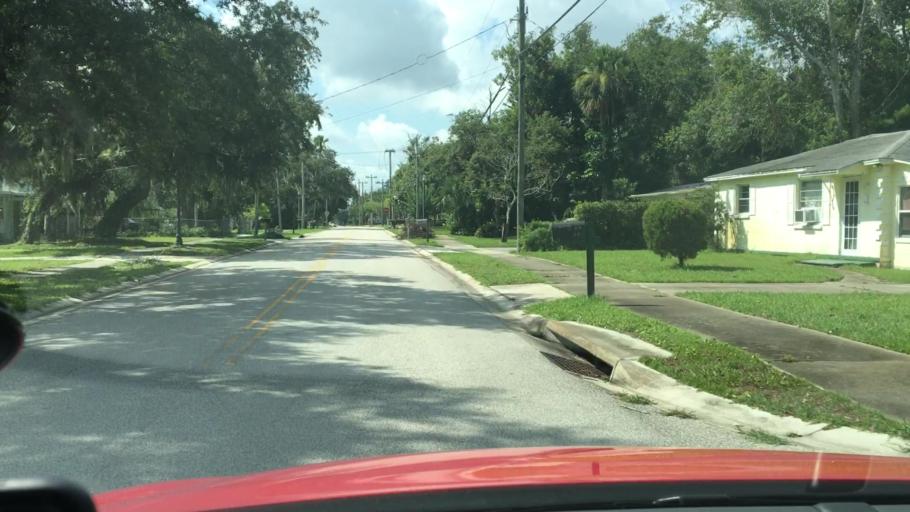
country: US
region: Florida
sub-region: Volusia County
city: Ormond Beach
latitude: 29.2777
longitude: -81.0555
